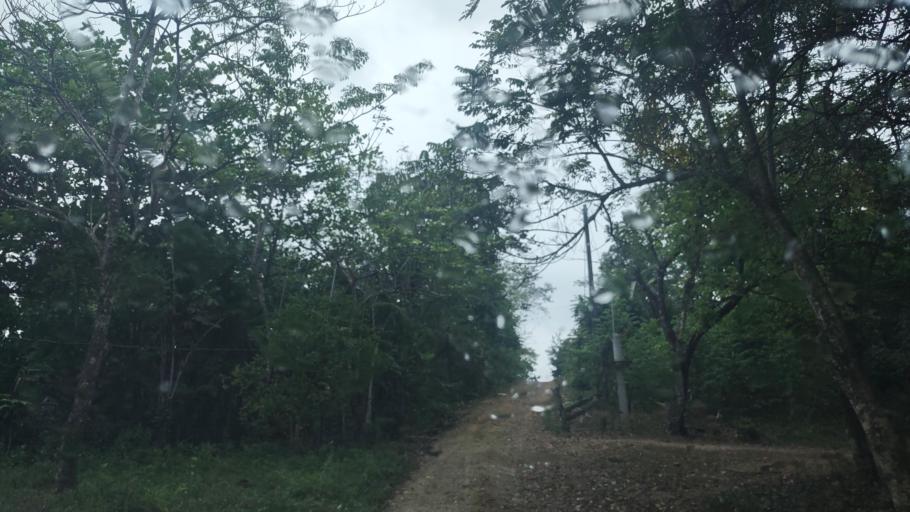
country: MX
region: Veracruz
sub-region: Uxpanapa
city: Poblado 10
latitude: 17.4480
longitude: -94.0971
